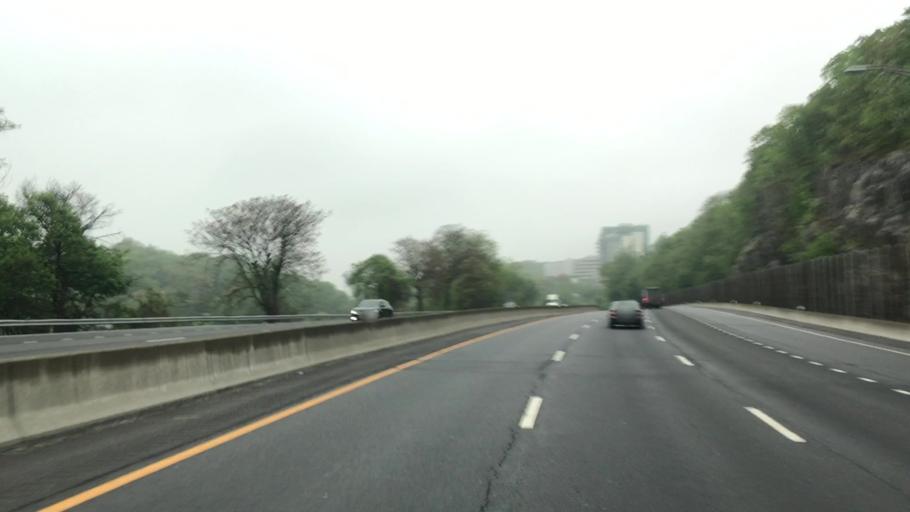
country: US
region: New York
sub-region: Westchester County
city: Tuckahoe
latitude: 40.9578
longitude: -73.8609
